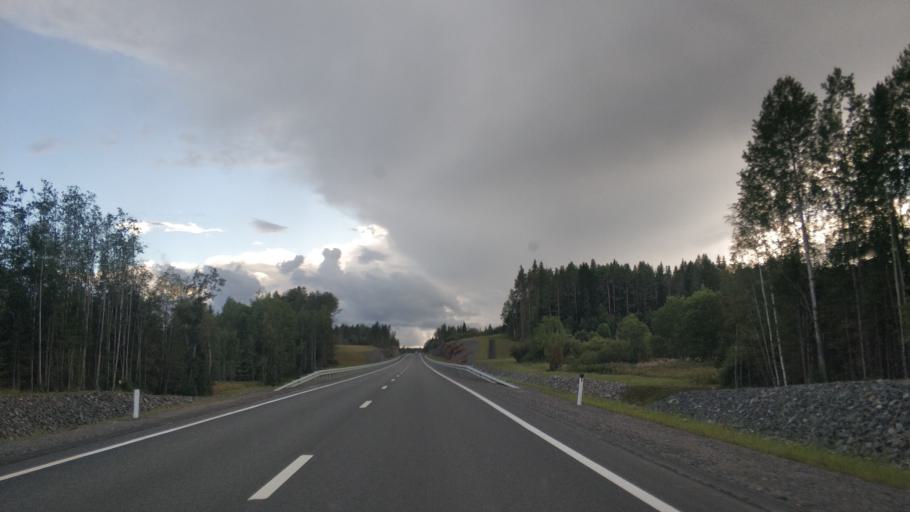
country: RU
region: Republic of Karelia
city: Lakhdenpokh'ya
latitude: 61.4393
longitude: 29.9828
